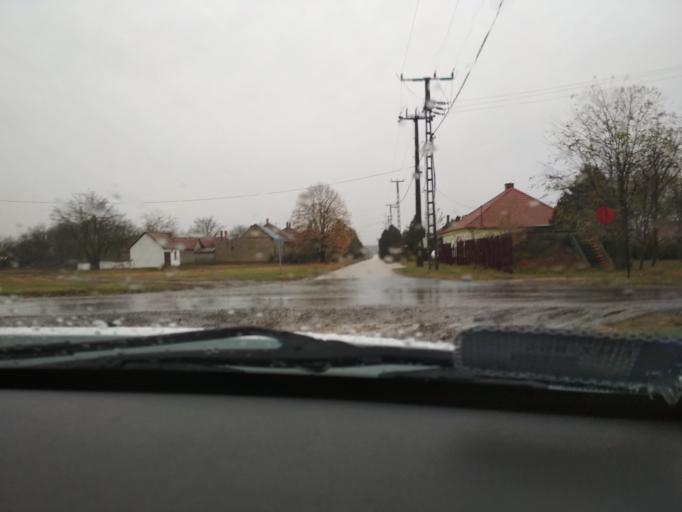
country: HU
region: Csongrad
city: Opusztaszer
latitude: 46.4400
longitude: 20.1332
